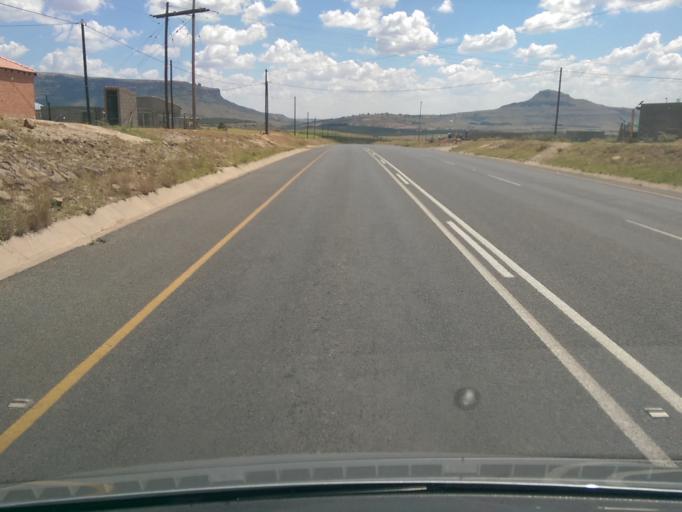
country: LS
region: Maseru
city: Maseru
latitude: -29.3965
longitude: 27.5192
